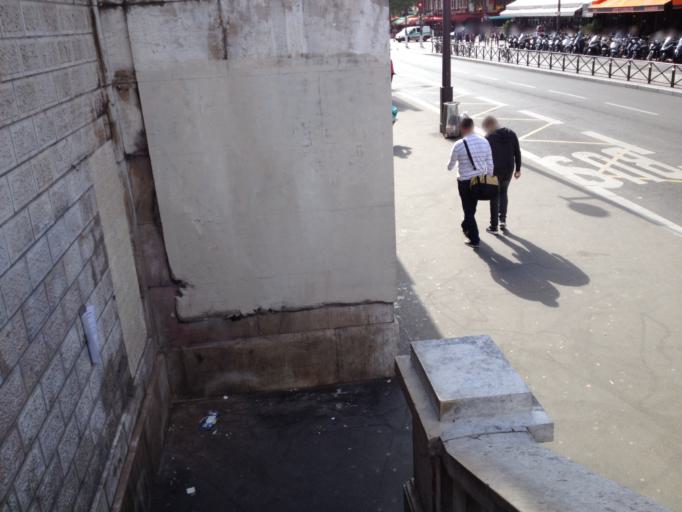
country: FR
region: Ile-de-France
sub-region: Paris
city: Paris
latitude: 48.8457
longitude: 2.3738
